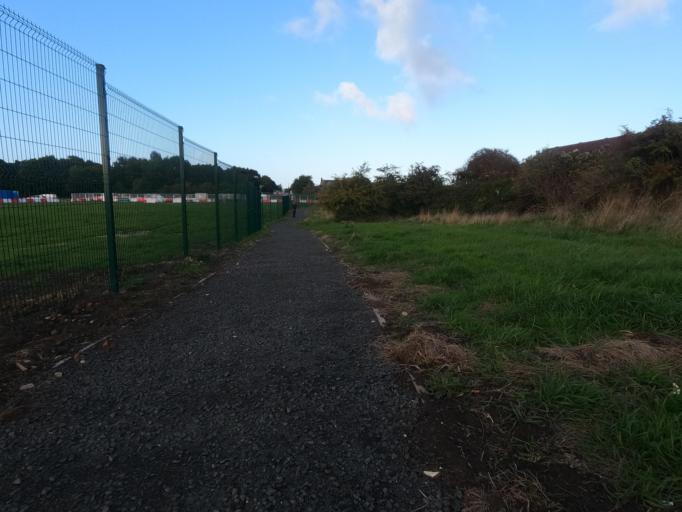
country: GB
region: England
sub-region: Northumberland
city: Seaton Delaval
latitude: 55.0737
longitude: -1.5374
